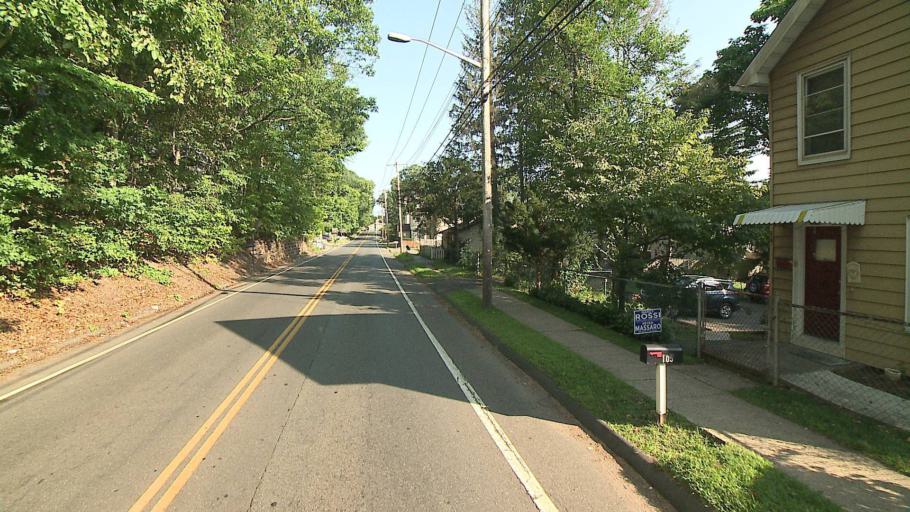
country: US
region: Connecticut
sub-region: New Haven County
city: West Haven
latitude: 41.2978
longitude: -72.9604
